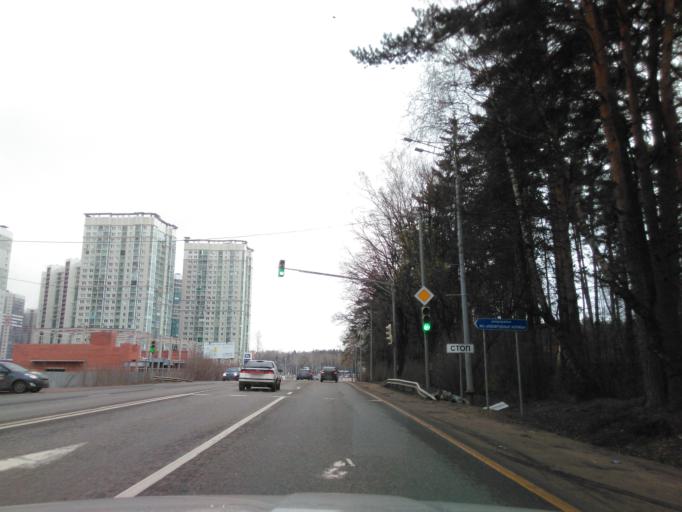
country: RU
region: Moskovskaya
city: Opalikha
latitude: 55.8356
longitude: 37.2641
